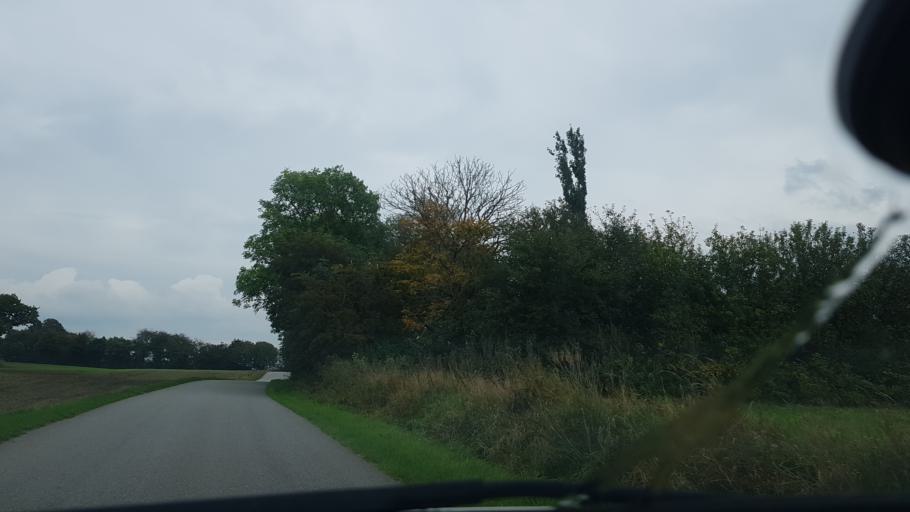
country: DK
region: South Denmark
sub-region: Vejle Kommune
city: Egtved
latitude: 55.5717
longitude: 9.2666
